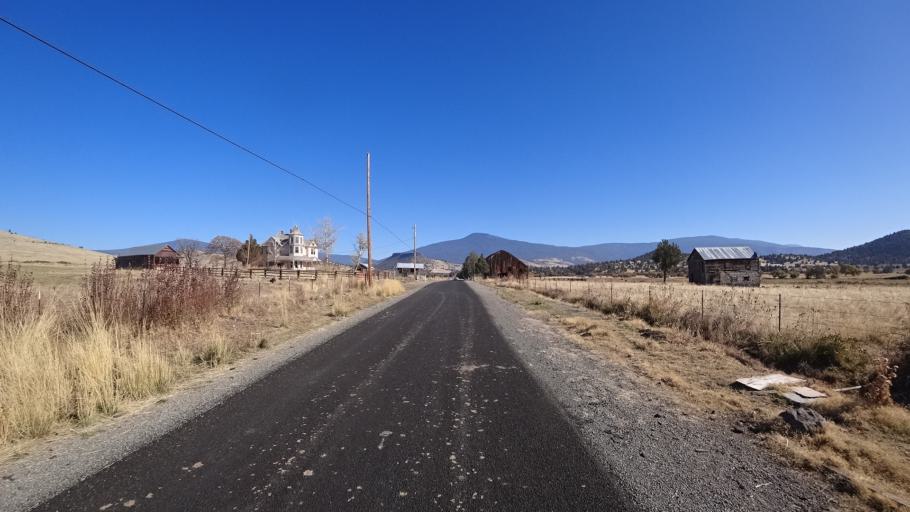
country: US
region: California
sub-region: Siskiyou County
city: Montague
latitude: 41.7262
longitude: -122.3827
